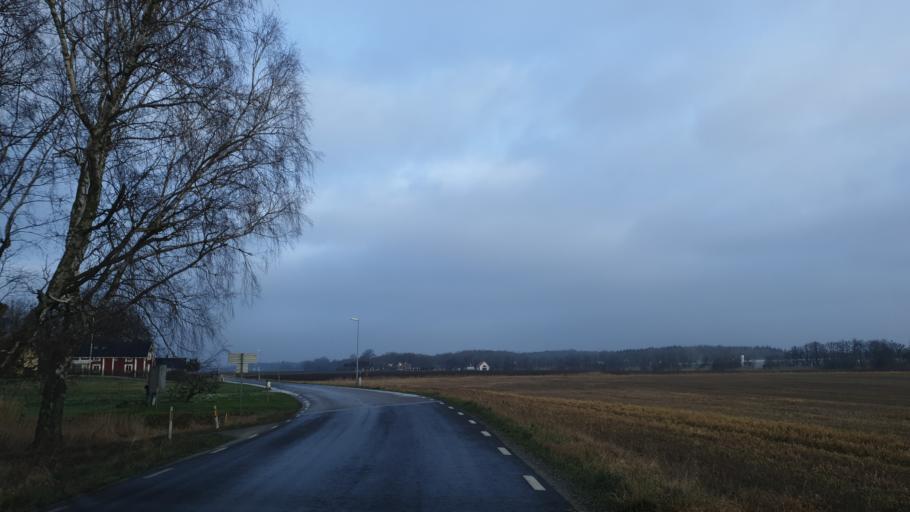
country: SE
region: Blekinge
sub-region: Karlshamns Kommun
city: Morrum
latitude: 56.1649
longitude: 14.7480
